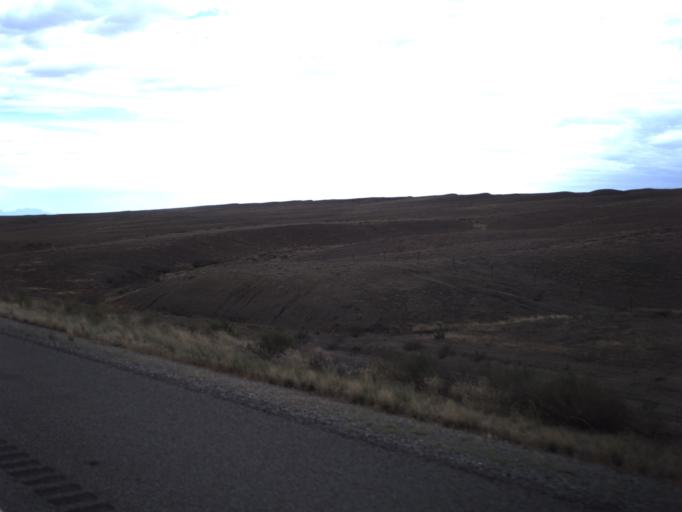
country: US
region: Utah
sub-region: Grand County
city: Moab
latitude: 38.9658
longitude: -110.0806
